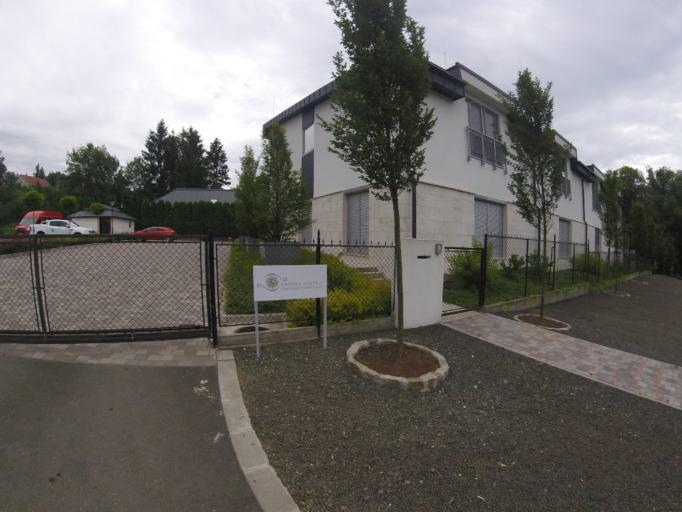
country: HU
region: Nograd
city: Romhany
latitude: 47.8724
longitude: 19.2477
